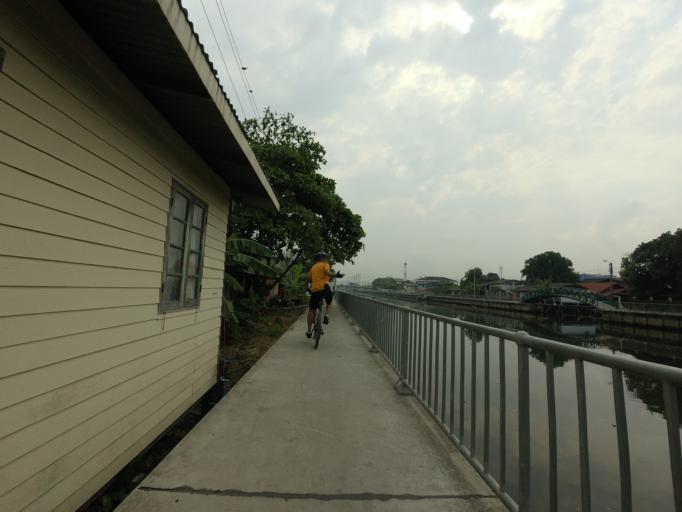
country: TH
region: Bangkok
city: Suan Luang
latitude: 13.7241
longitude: 100.6785
